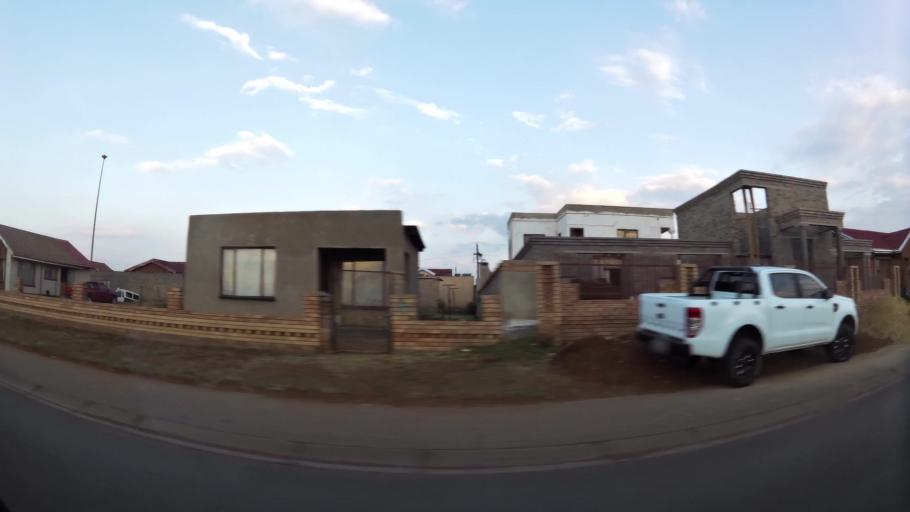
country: ZA
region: Gauteng
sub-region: City of Johannesburg Metropolitan Municipality
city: Orange Farm
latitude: -26.5602
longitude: 27.8551
